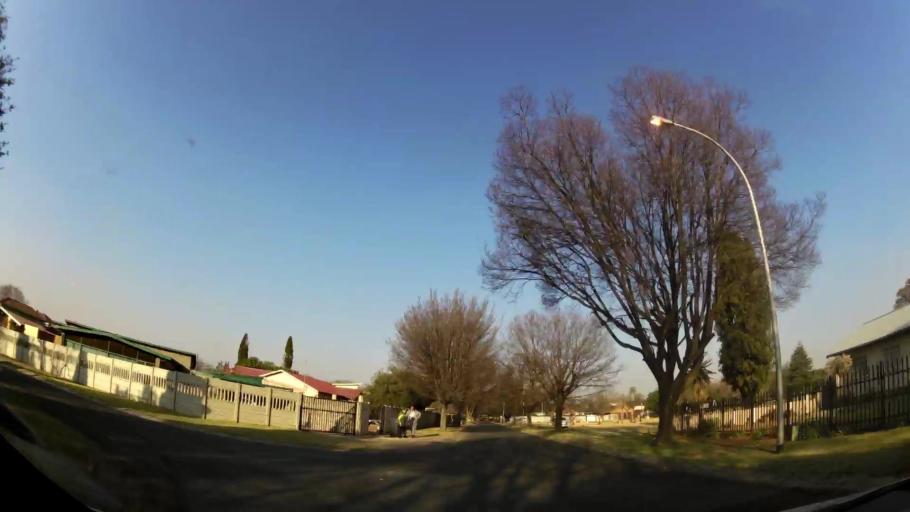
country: ZA
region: Gauteng
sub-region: Ekurhuleni Metropolitan Municipality
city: Springs
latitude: -26.2539
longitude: 28.3881
